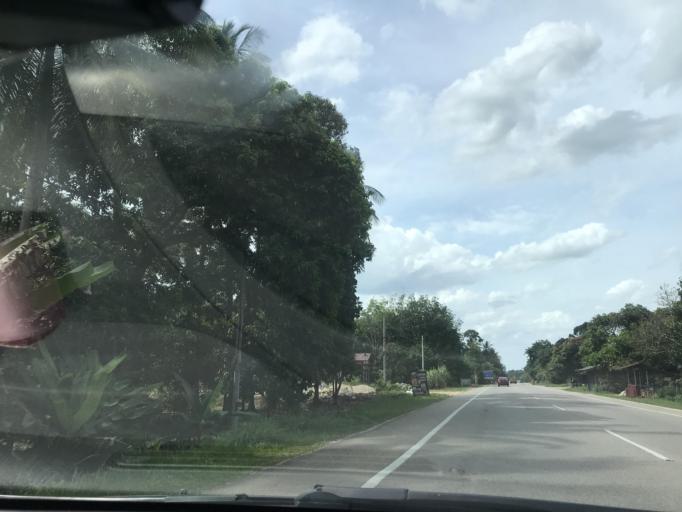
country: MY
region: Kelantan
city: Kampong Pangkal Kalong
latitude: 5.8934
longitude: 102.1828
